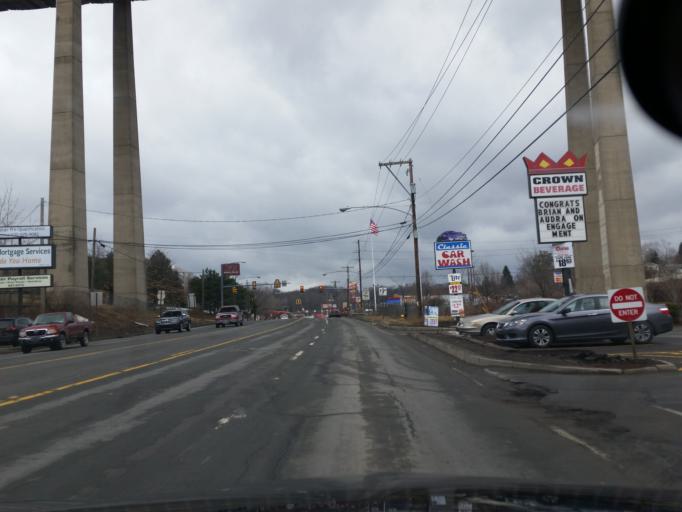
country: US
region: Pennsylvania
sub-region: Lackawanna County
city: Clarks Green
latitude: 41.4831
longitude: -75.6907
